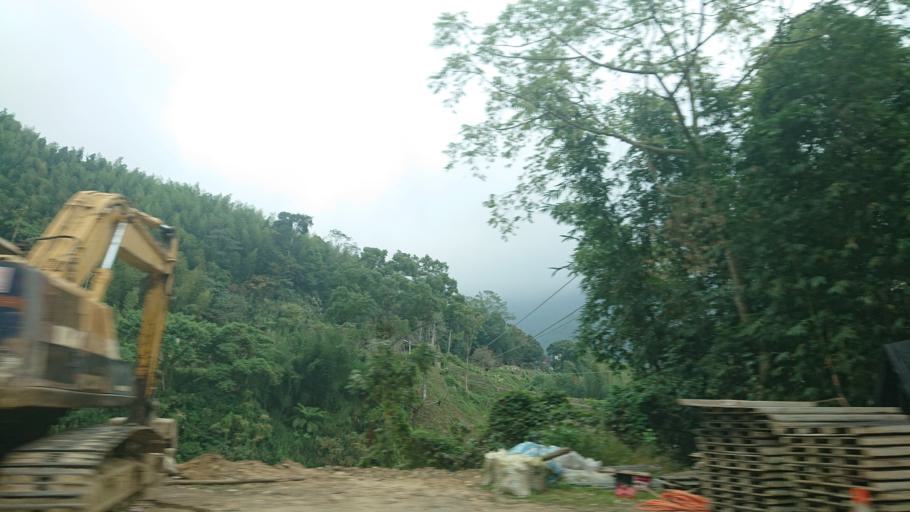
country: TW
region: Taiwan
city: Lugu
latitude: 23.6088
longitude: 120.7097
